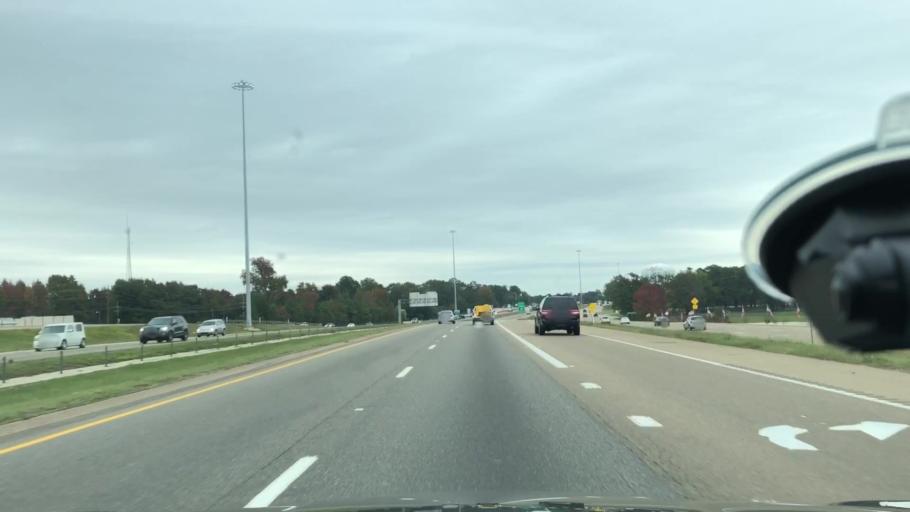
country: US
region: Arkansas
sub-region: Miller County
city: Texarkana
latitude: 33.4668
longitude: -94.0631
